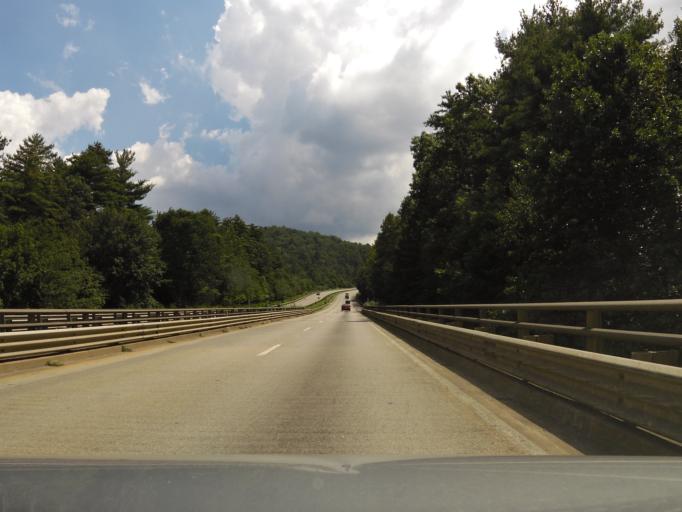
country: US
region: North Carolina
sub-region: Henderson County
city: East Flat Rock
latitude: 35.2737
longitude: -82.3730
